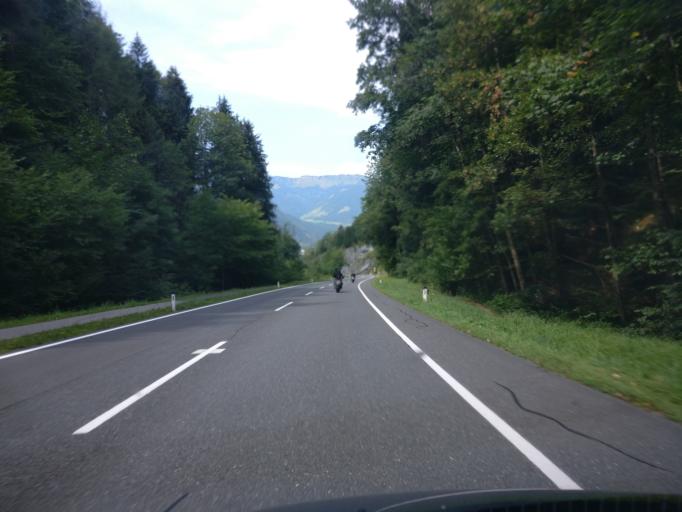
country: AT
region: Salzburg
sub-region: Politischer Bezirk Hallein
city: Golling an der Salzach
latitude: 47.5791
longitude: 13.1895
